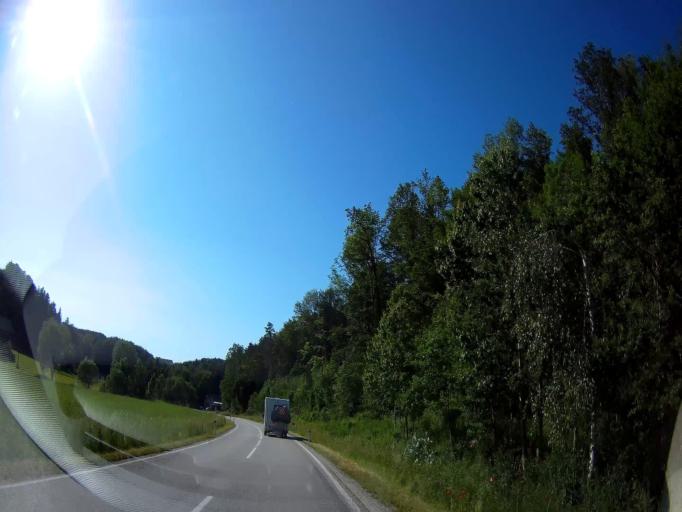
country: DE
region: Bavaria
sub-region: Lower Bavaria
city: Kirchdorf am Inn
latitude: 48.1392
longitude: 13.0182
